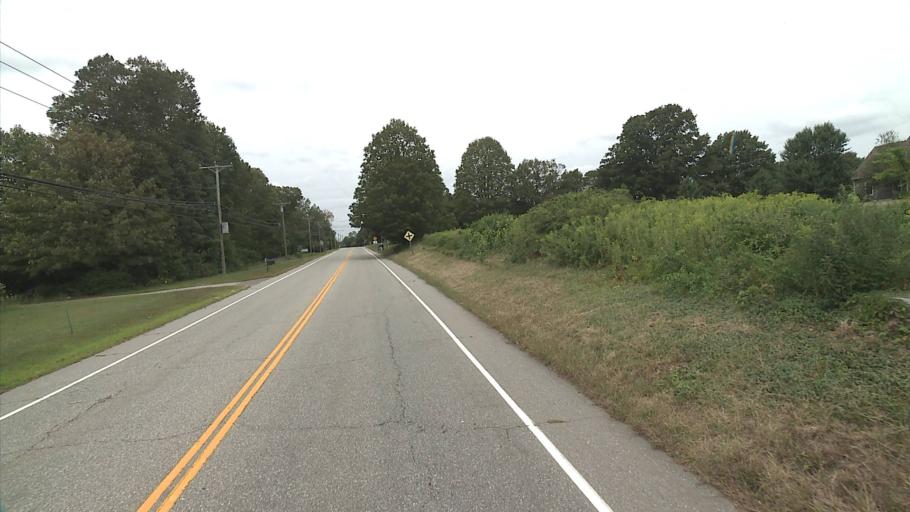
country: US
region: Connecticut
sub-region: Tolland County
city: Hebron
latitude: 41.6783
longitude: -72.4116
